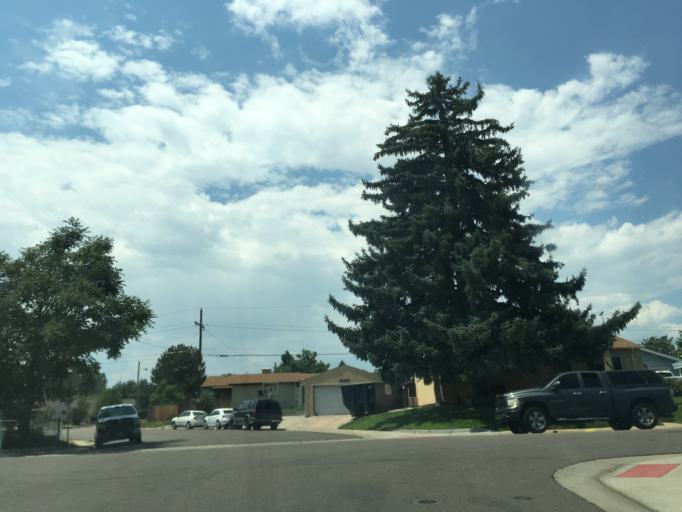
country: US
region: Colorado
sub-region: Arapahoe County
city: Sheridan
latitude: 39.6877
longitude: -105.0323
